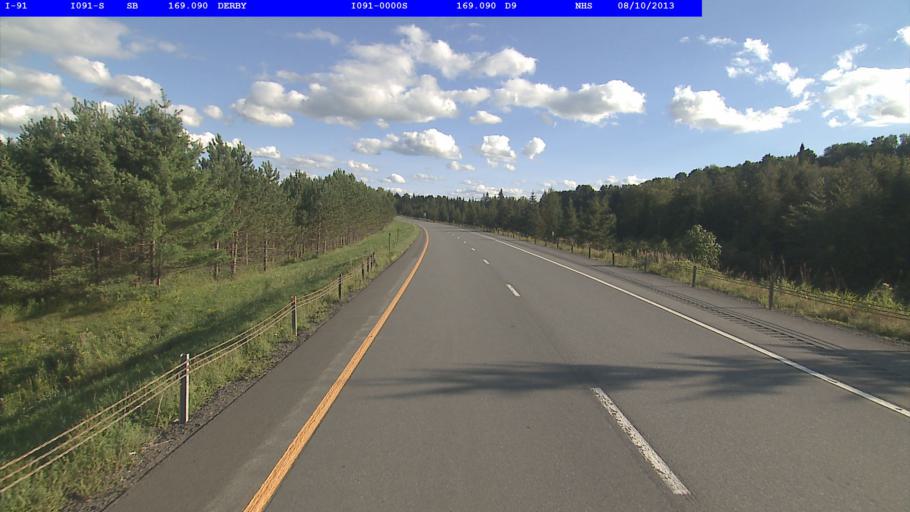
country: US
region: Vermont
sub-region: Orleans County
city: Newport
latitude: 44.9094
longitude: -72.1789
